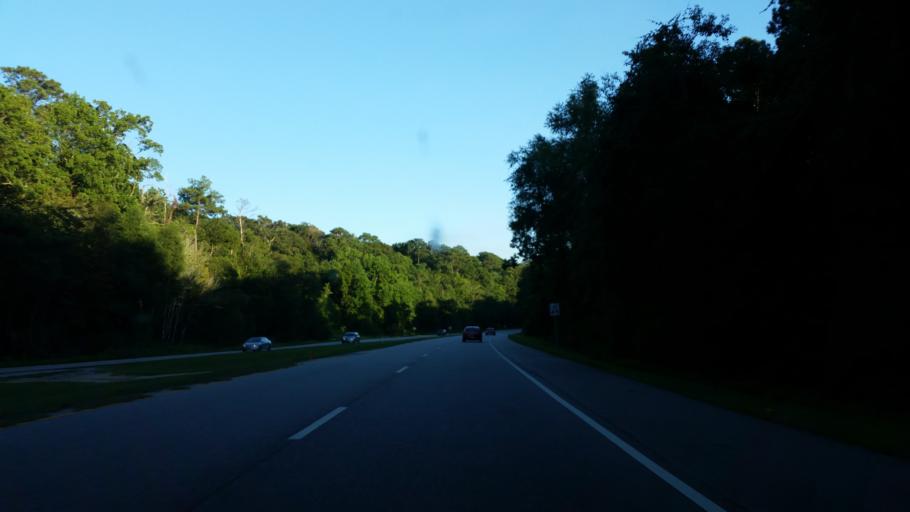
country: US
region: Alabama
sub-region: Baldwin County
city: Spanish Fort
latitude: 30.6650
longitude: -87.9160
